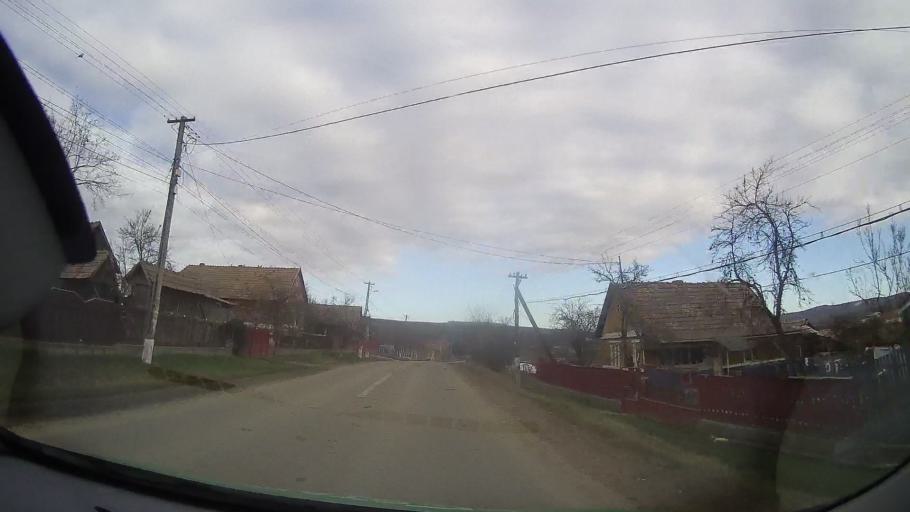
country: RO
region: Mures
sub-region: Comuna Iernut
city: Iernut
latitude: 46.4788
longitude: 24.2283
